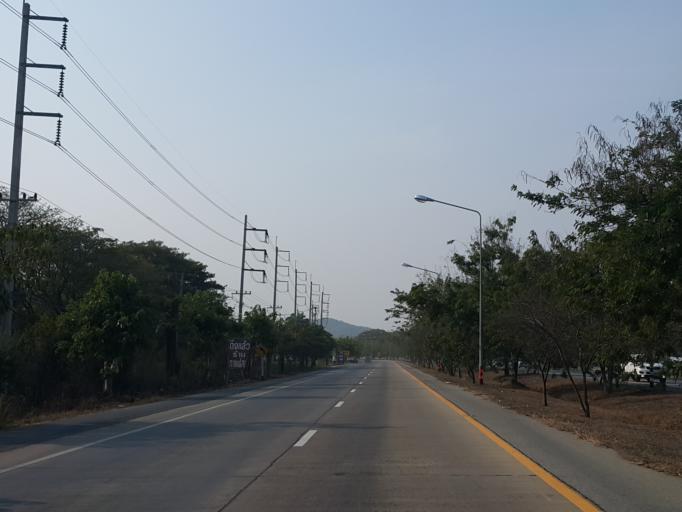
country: TH
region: Suphan Buri
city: Doembang Nangbuat
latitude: 14.8273
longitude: 100.1143
